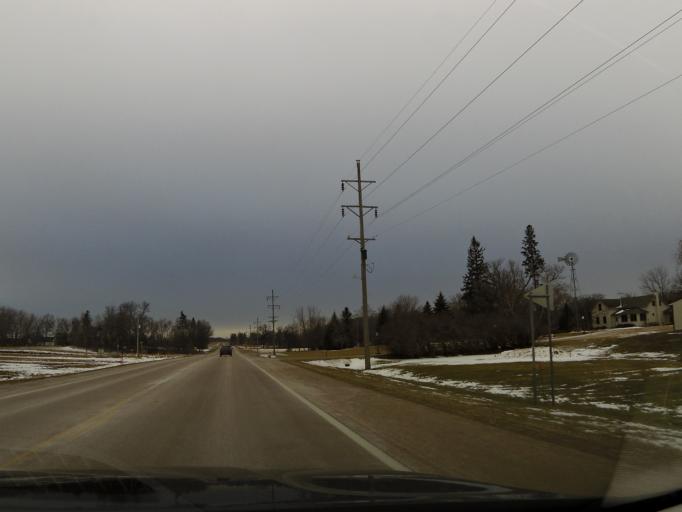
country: US
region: Minnesota
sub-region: Carver County
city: Watertown
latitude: 44.9212
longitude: -93.8287
